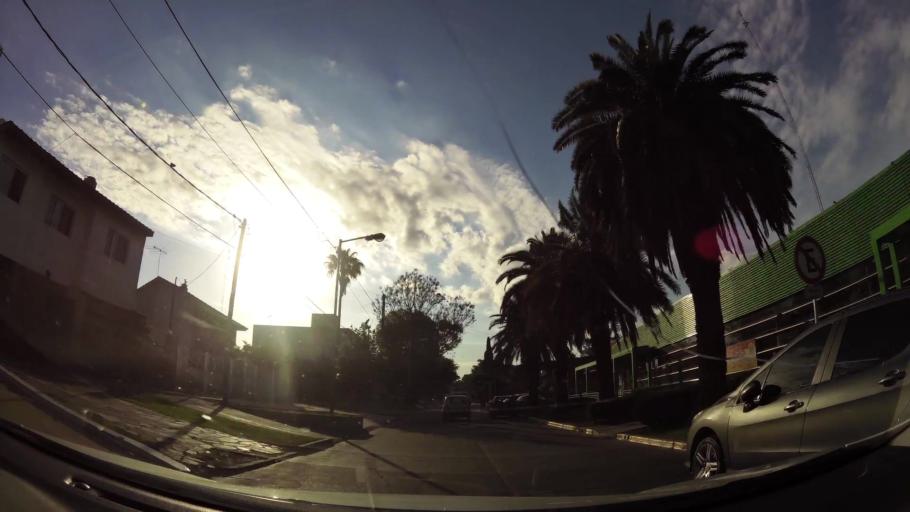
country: AR
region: Buenos Aires
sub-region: Partido de Tigre
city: Tigre
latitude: -34.4561
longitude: -58.6275
